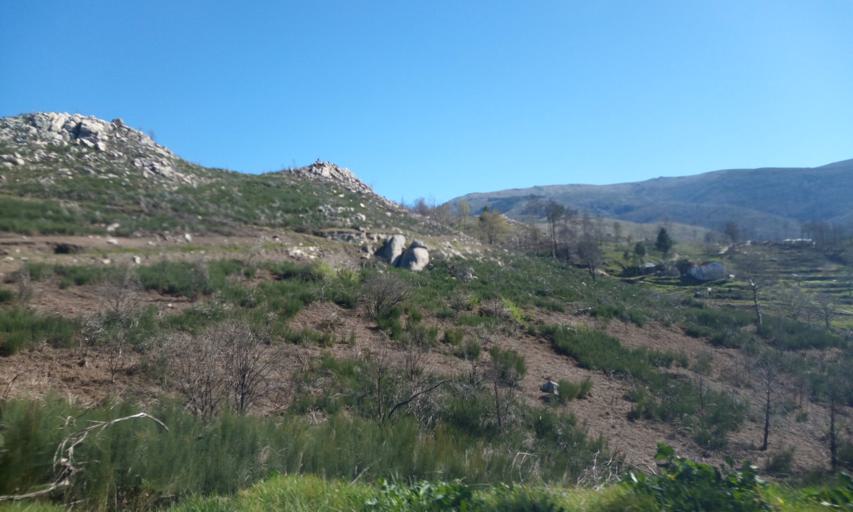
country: PT
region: Guarda
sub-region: Manteigas
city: Manteigas
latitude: 40.4916
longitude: -7.5779
